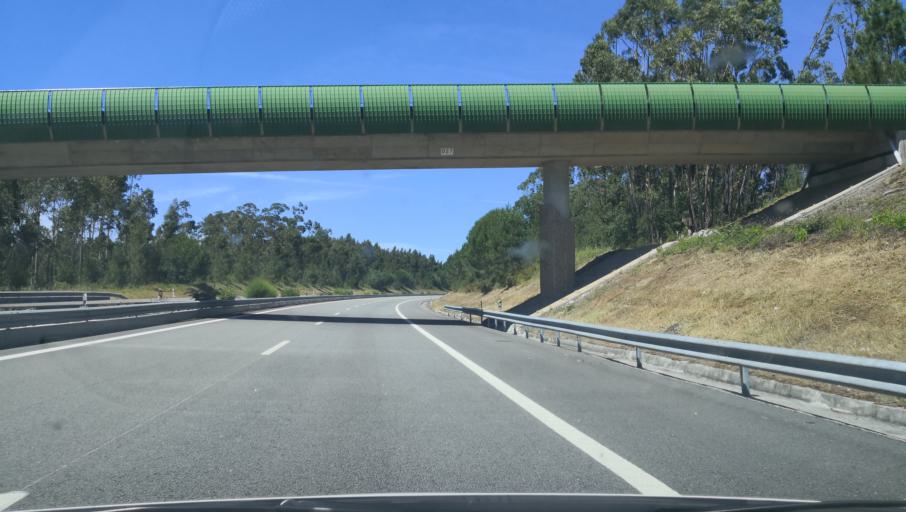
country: PT
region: Coimbra
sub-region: Montemor-O-Velho
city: Montemor-o-Velho
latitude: 40.2170
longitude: -8.6753
